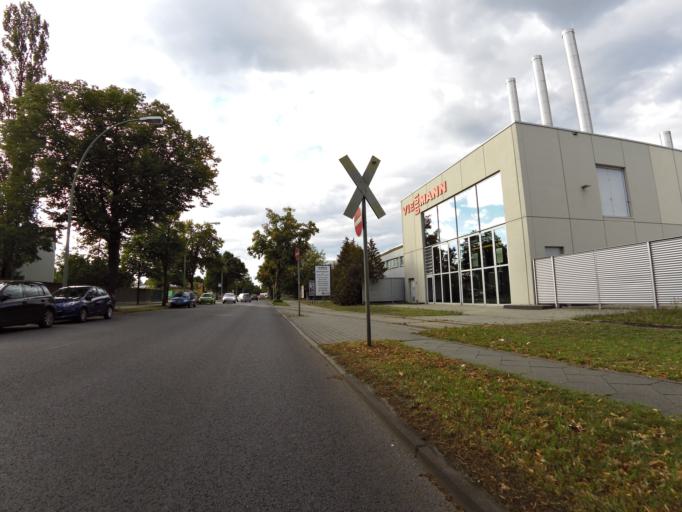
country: DE
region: Berlin
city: Rudow
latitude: 52.4308
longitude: 13.4974
